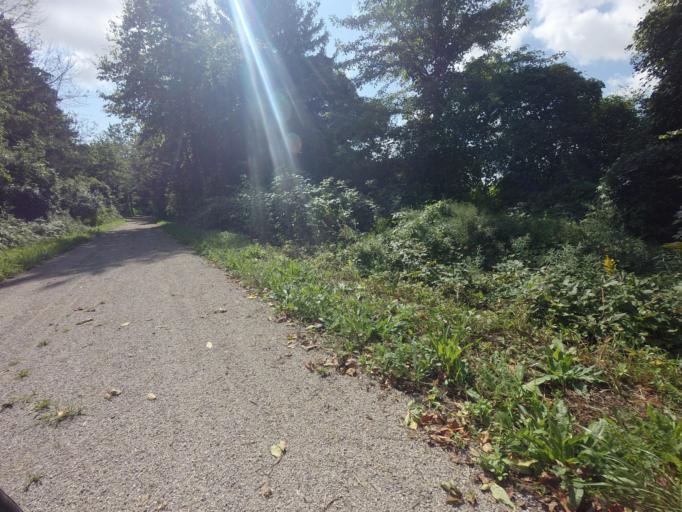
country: CA
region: Ontario
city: Huron East
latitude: 43.6792
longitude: -81.2970
